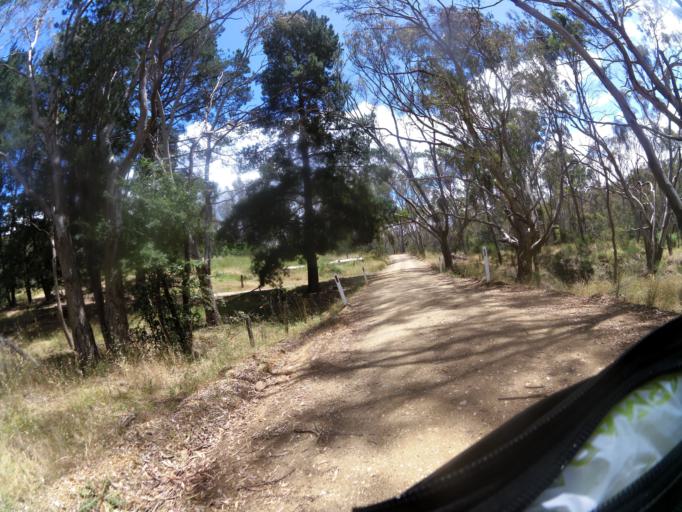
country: AU
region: Victoria
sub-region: Mount Alexander
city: Castlemaine
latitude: -37.0580
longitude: 144.2720
